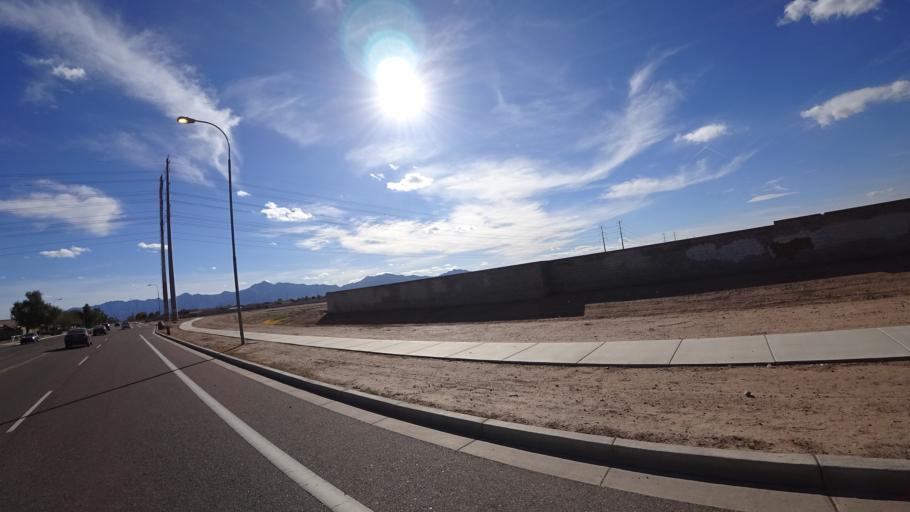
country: US
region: Arizona
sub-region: Maricopa County
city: Tolleson
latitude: 33.4167
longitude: -112.2213
